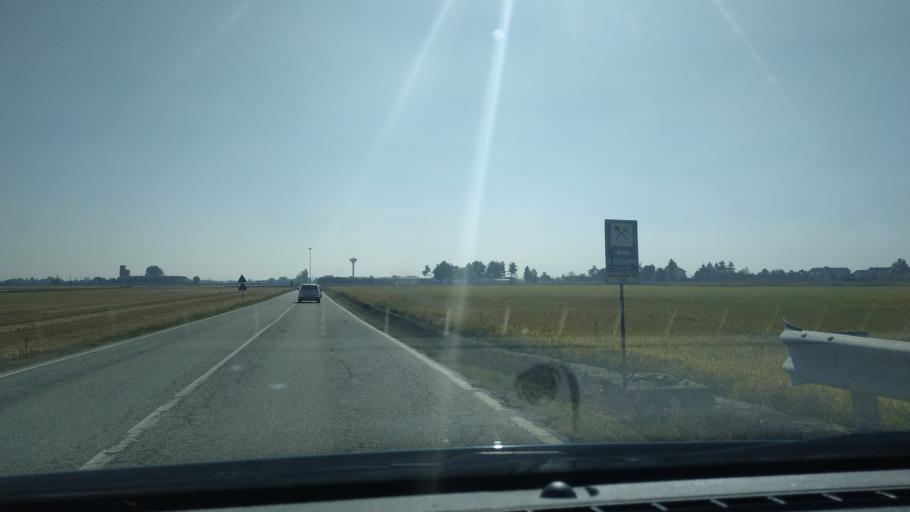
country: IT
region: Piedmont
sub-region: Provincia di Alessandria
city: Borgo San Martino
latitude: 45.1031
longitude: 8.5231
